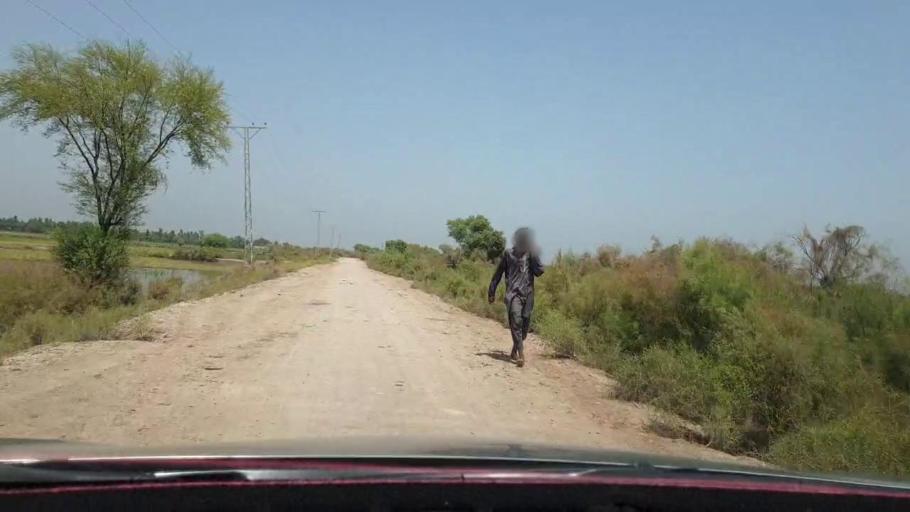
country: PK
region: Sindh
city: Warah
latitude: 27.4015
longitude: 67.6898
